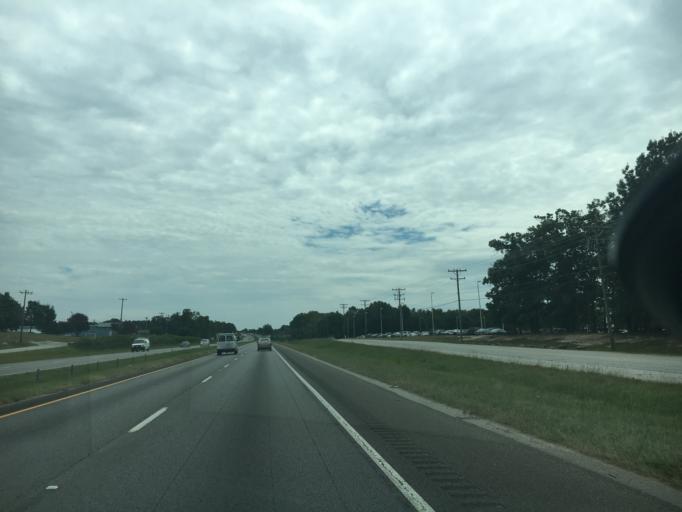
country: US
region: South Carolina
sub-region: Greenville County
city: Fountain Inn
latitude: 34.6741
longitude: -82.1926
